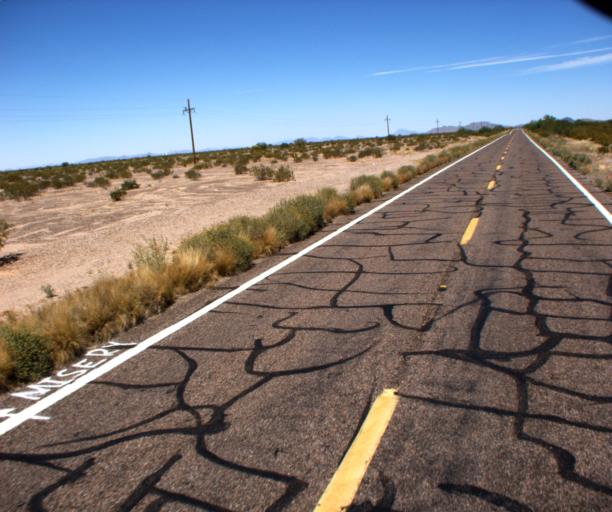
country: US
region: Arizona
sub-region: Pima County
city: Ajo
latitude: 32.6365
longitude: -112.8638
